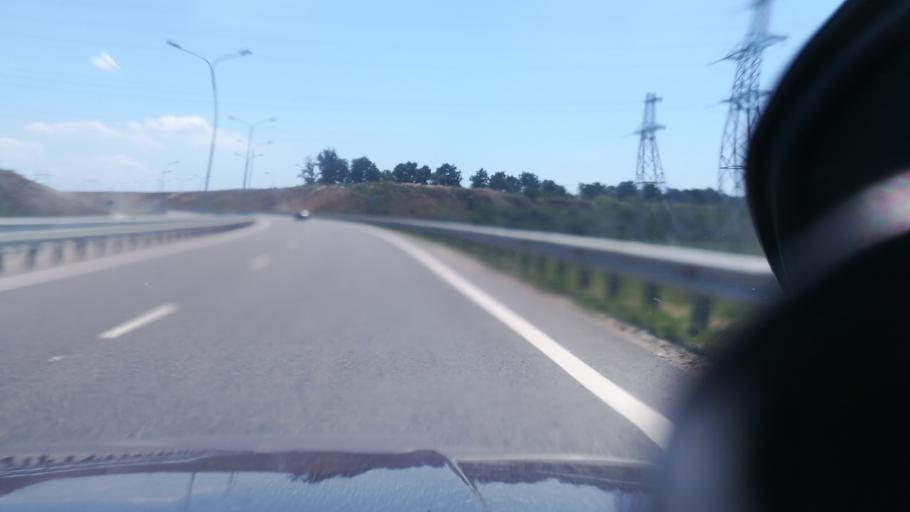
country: RU
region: Krasnodarskiy
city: Dzhiginka
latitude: 45.1276
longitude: 37.3106
